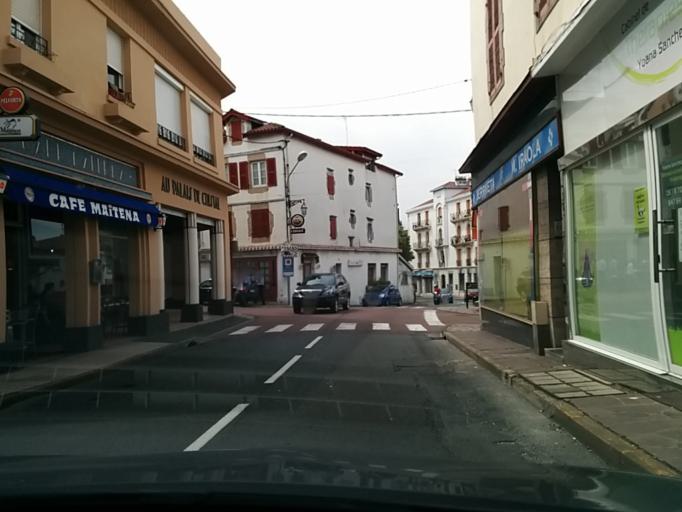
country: FR
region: Aquitaine
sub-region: Departement des Pyrenees-Atlantiques
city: Hendaye
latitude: 43.3585
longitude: -1.7761
